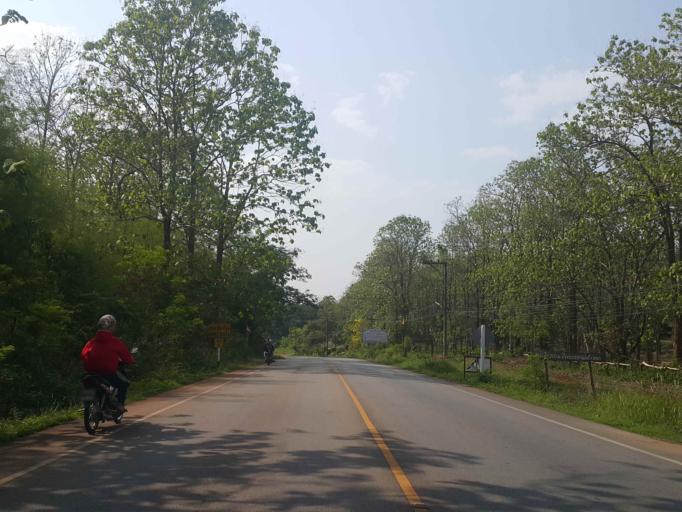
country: TH
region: Chiang Mai
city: Mae Taeng
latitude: 19.0935
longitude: 99.0839
